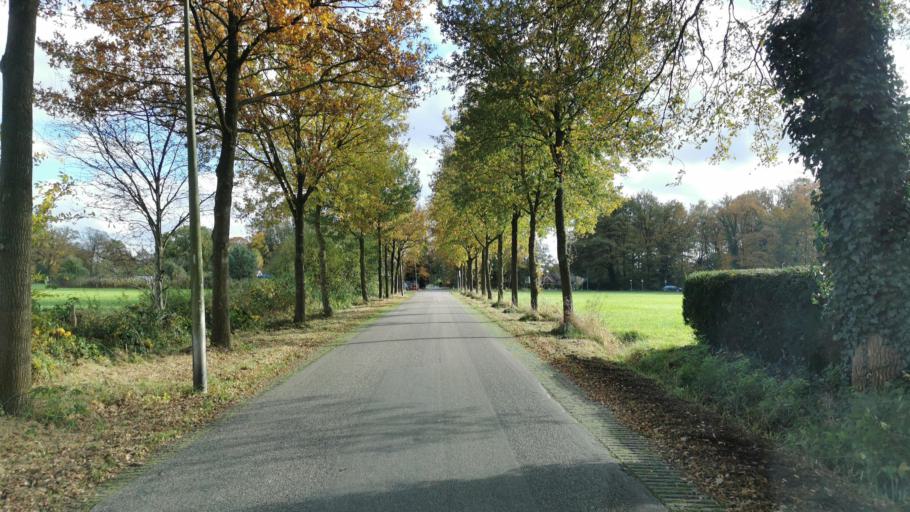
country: NL
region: Overijssel
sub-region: Gemeente Enschede
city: Enschede
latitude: 52.1990
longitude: 6.9171
